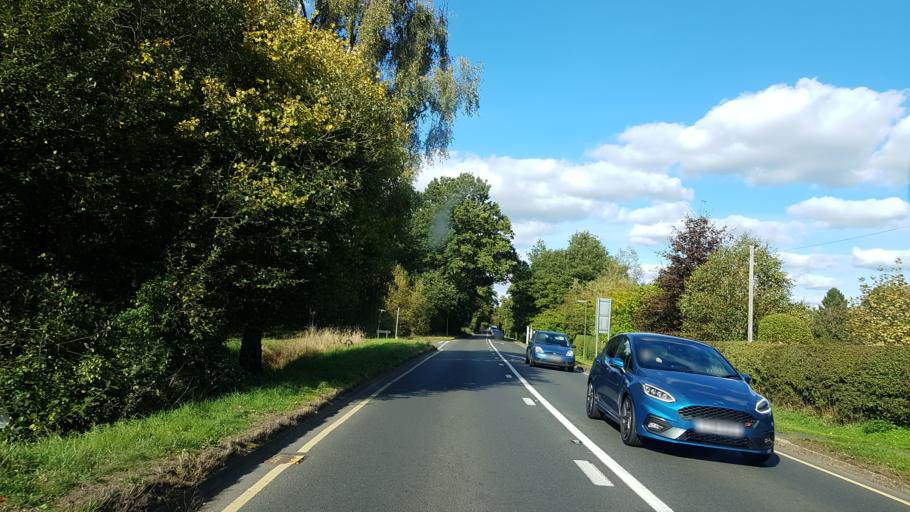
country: GB
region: England
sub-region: Surrey
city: Milford
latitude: 51.1635
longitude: -0.6503
